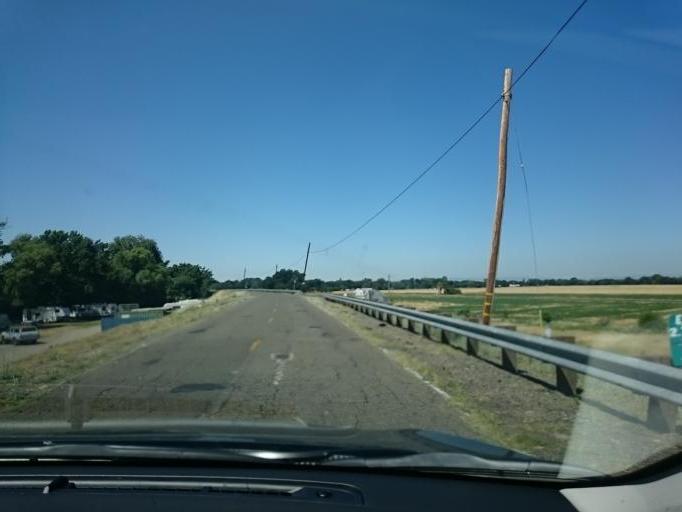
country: US
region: California
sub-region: Yolo County
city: West Sacramento
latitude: 38.5331
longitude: -121.5290
